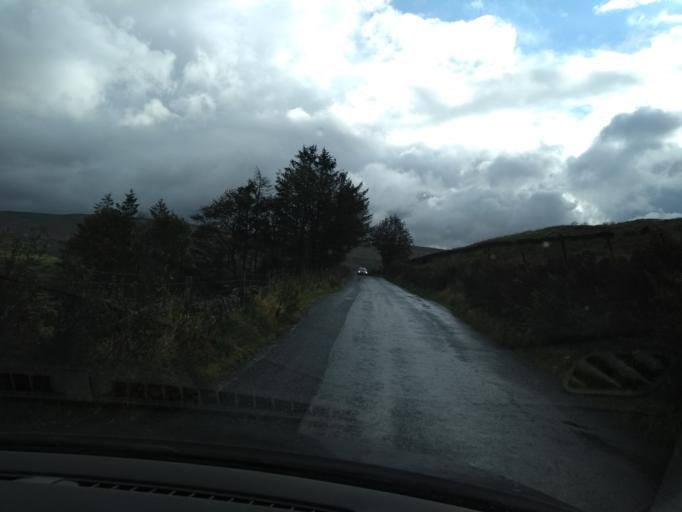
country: GB
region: England
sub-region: Cumbria
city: Kirkby Stephen
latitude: 54.3859
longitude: -2.1733
